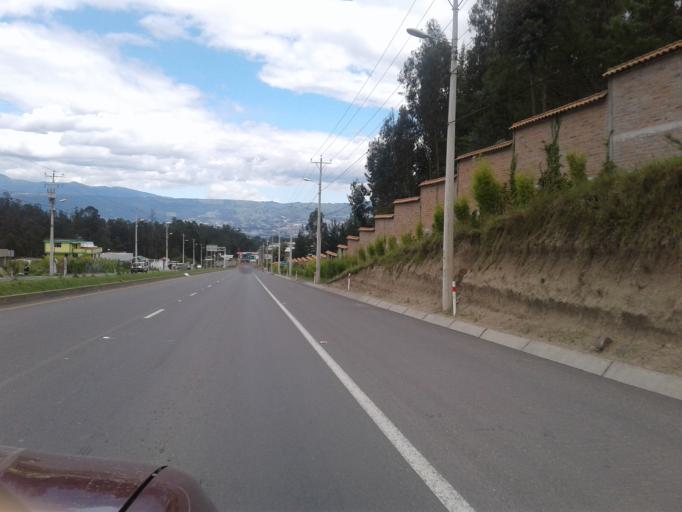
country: EC
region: Pichincha
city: Sangolqui
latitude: -0.3283
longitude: -78.3903
